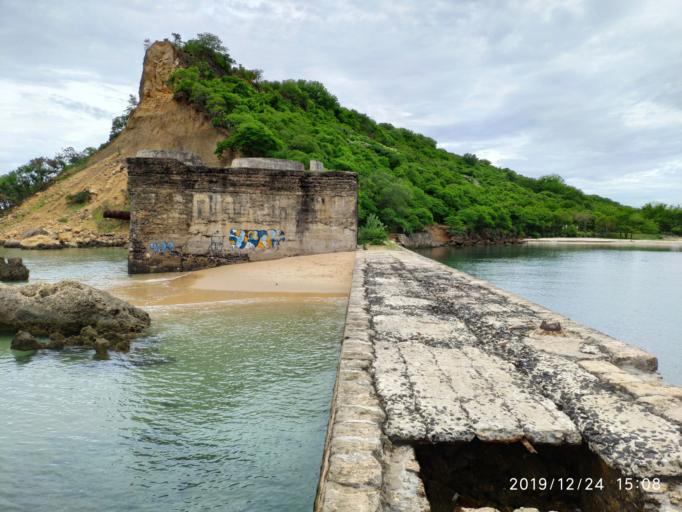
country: MG
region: Diana
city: Antsiranana
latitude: -12.2584
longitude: 49.3290
